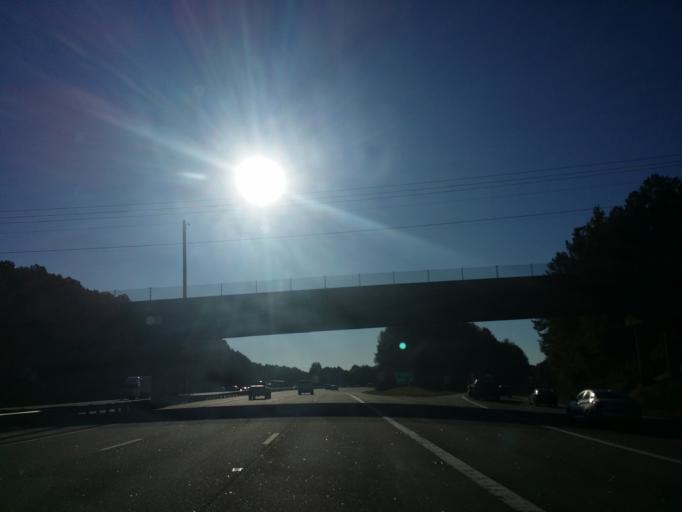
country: US
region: North Carolina
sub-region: Wake County
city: Cary
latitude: 35.8202
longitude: -78.7436
